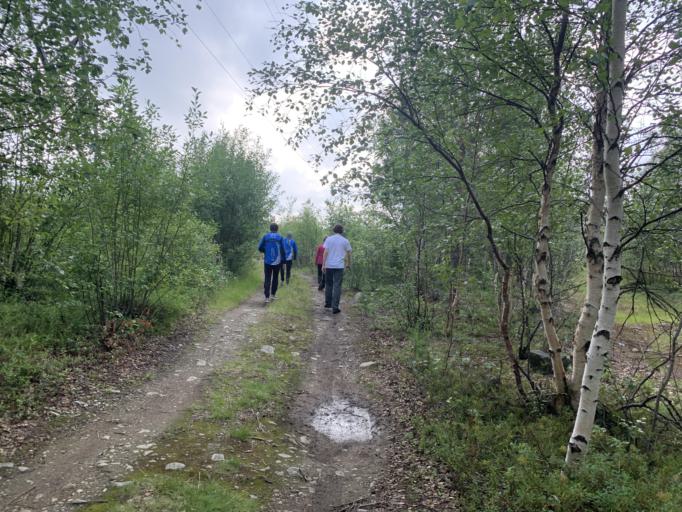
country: RU
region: Murmansk
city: Monchegorsk
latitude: 67.7972
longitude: 32.7901
